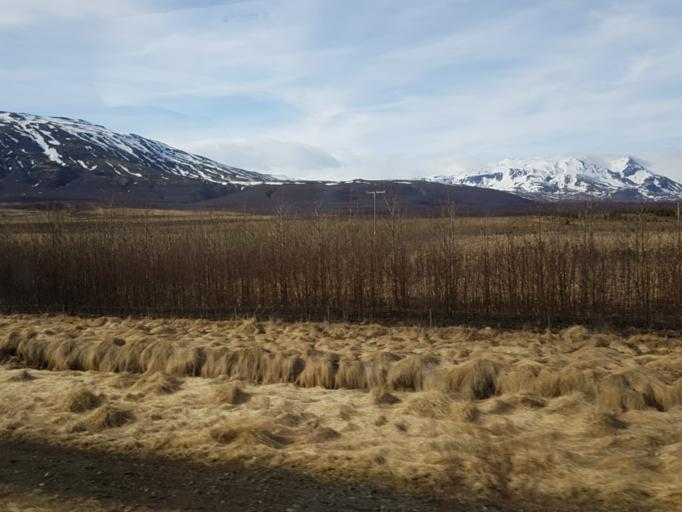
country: IS
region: South
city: Selfoss
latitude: 64.2404
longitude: -20.5138
